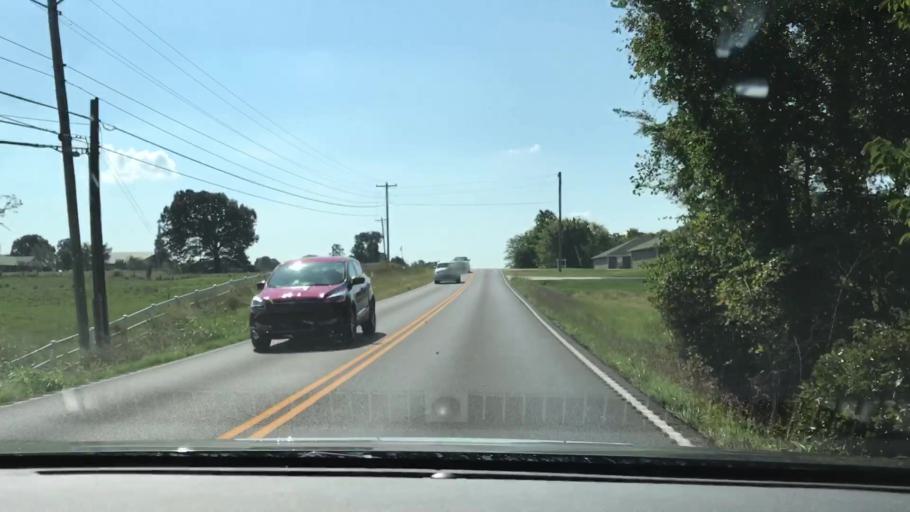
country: US
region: Kentucky
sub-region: Marshall County
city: Benton
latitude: 36.8198
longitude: -88.3503
